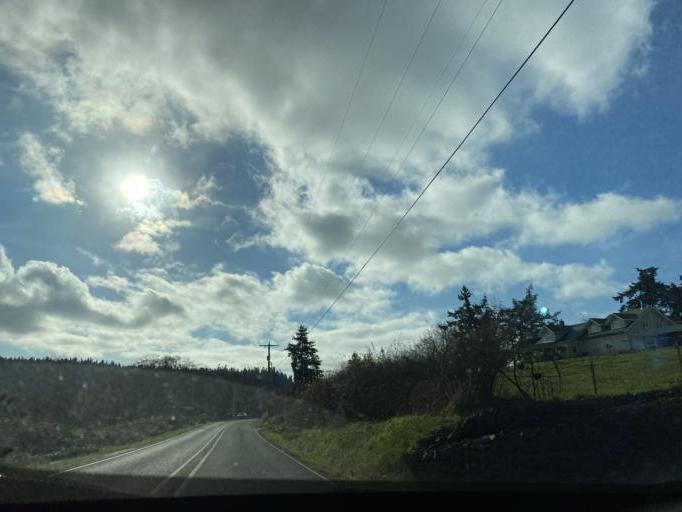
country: US
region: Washington
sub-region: Island County
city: Langley
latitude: 47.9477
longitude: -122.4385
